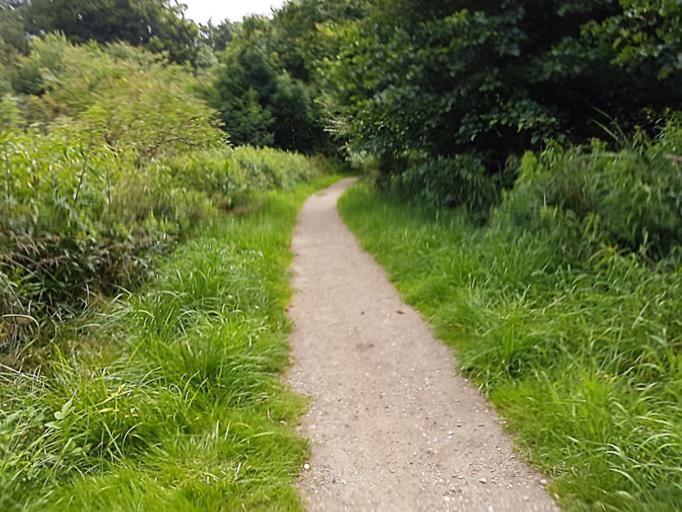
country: DK
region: Capital Region
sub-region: Fureso Kommune
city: Farum
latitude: 55.7984
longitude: 12.3679
